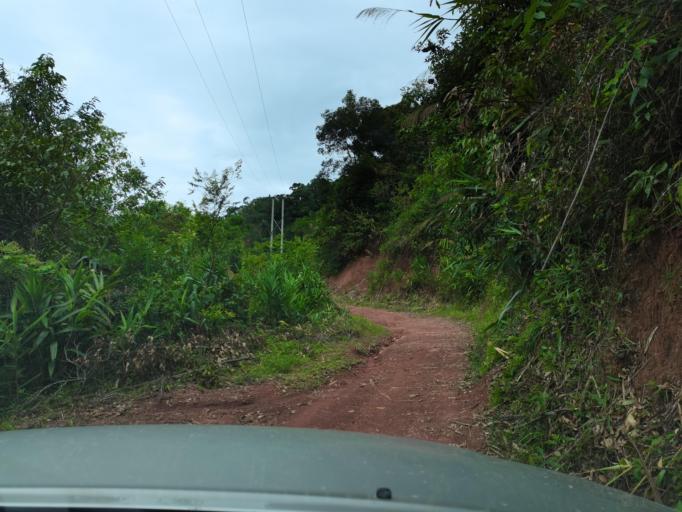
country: LA
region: Loungnamtha
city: Muang Nale
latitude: 20.5087
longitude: 101.0820
